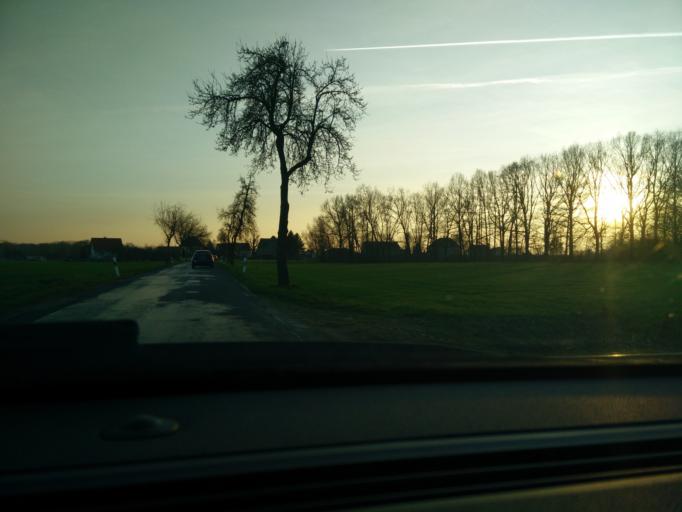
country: DE
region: Saxony
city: Kitzscher
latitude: 51.1804
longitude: 12.5308
